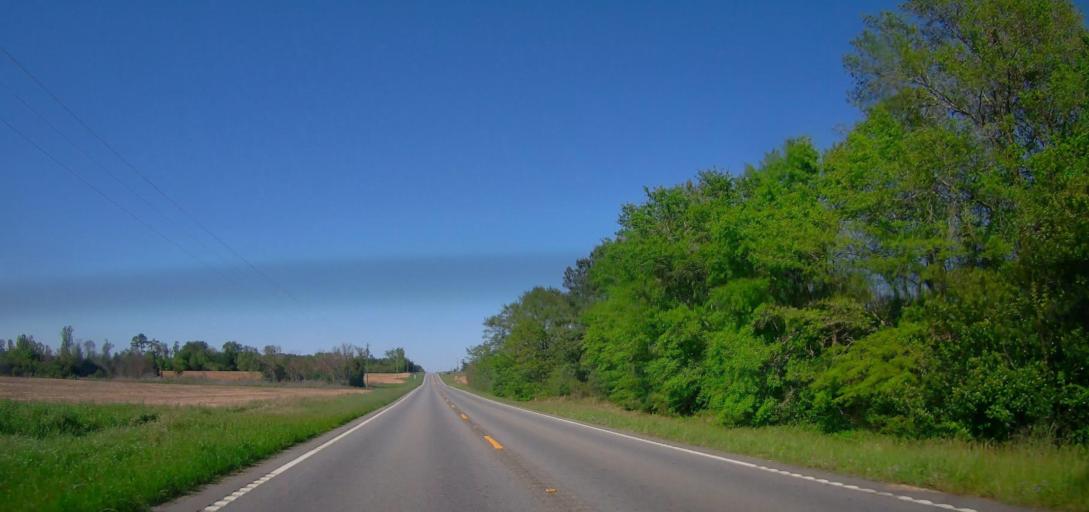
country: US
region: Georgia
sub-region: Pulaski County
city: Hawkinsville
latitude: 32.1867
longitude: -83.5029
